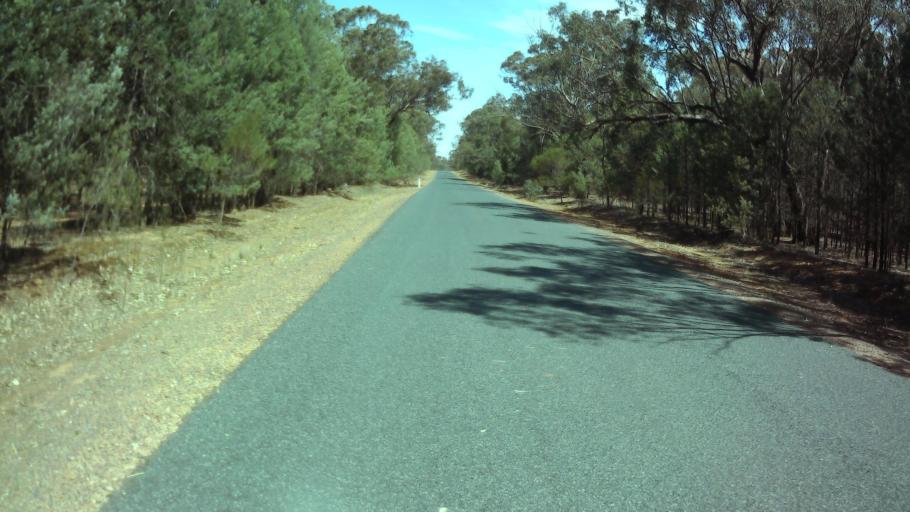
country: AU
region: New South Wales
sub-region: Weddin
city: Grenfell
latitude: -34.0712
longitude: 148.1402
